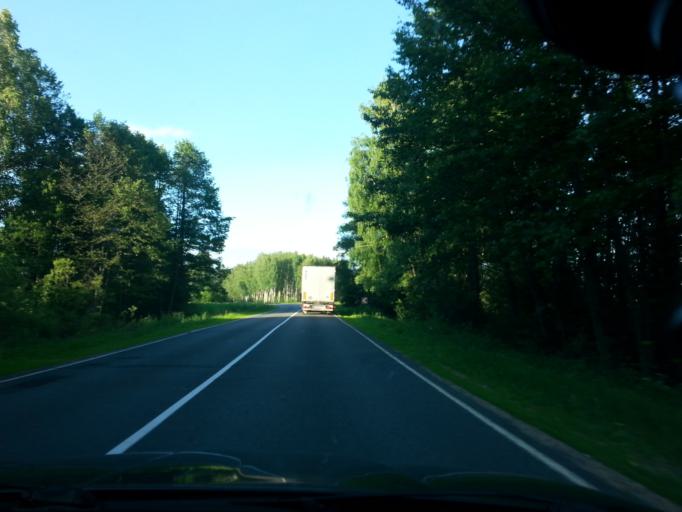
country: BY
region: Minsk
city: Svir
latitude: 54.8800
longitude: 26.3679
